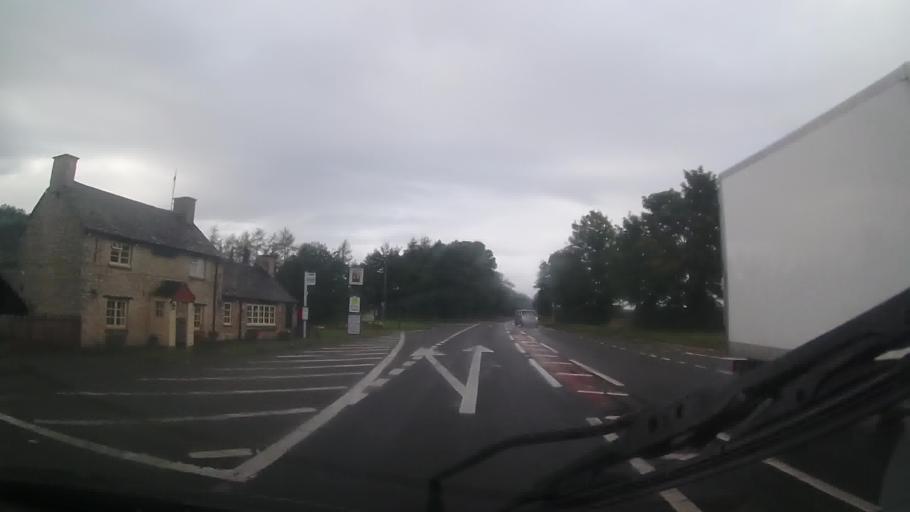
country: GB
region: England
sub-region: Oxfordshire
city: Woodstock
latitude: 51.8690
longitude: -1.3776
